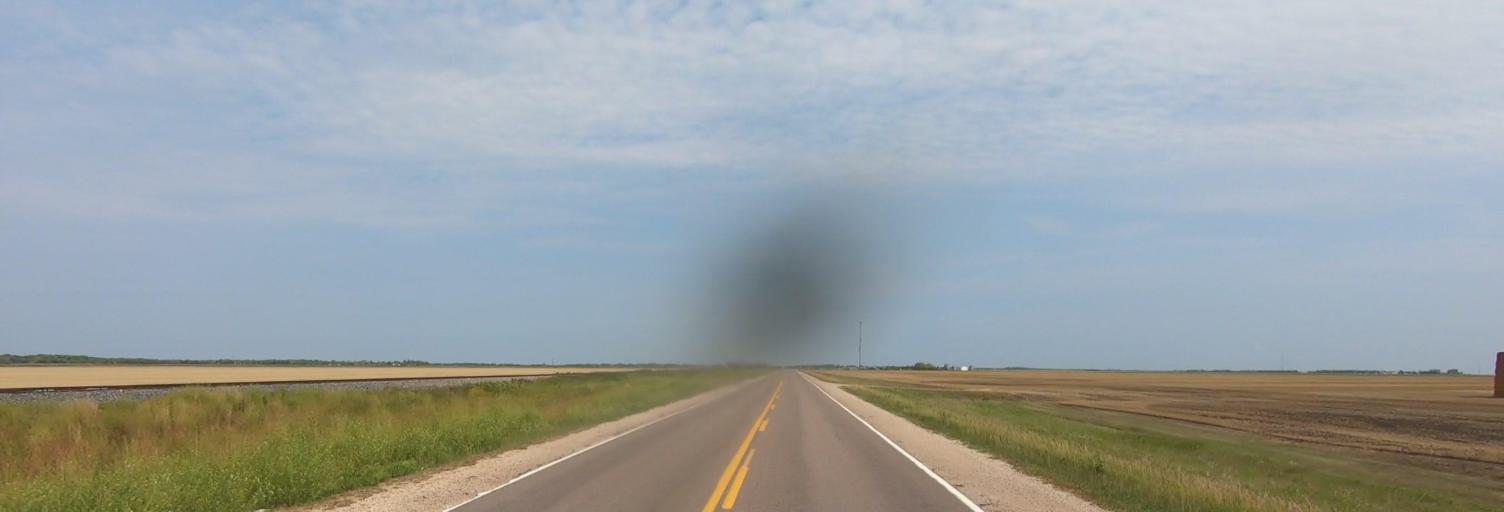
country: CA
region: Manitoba
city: Headingley
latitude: 49.6592
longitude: -97.2885
